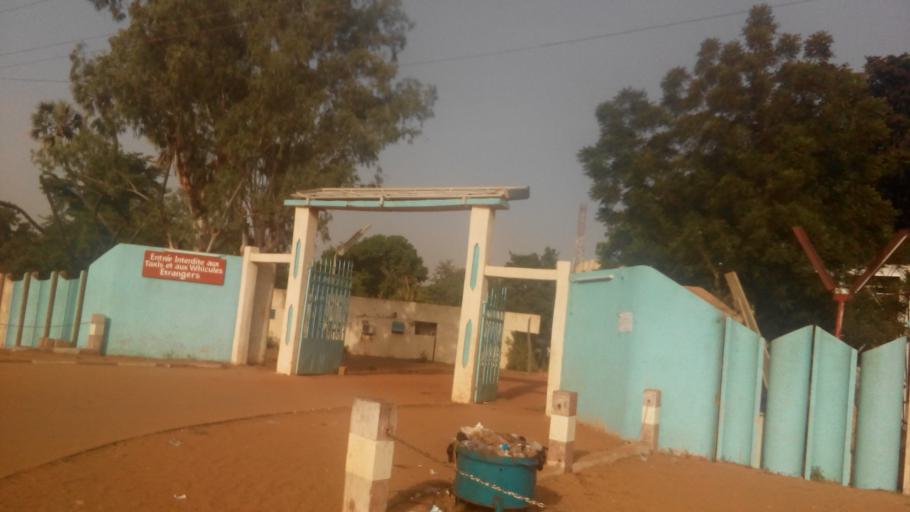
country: NE
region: Niamey
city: Niamey
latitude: 13.5006
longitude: 2.0998
